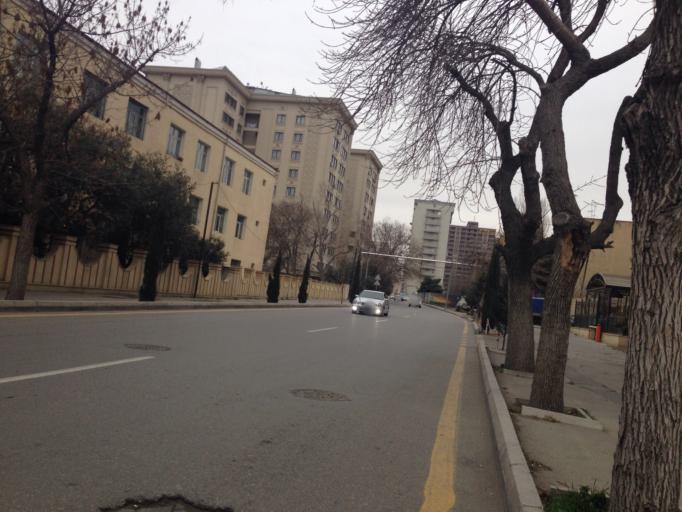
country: AZ
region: Baki
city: Baku
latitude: 40.3796
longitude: 49.8641
